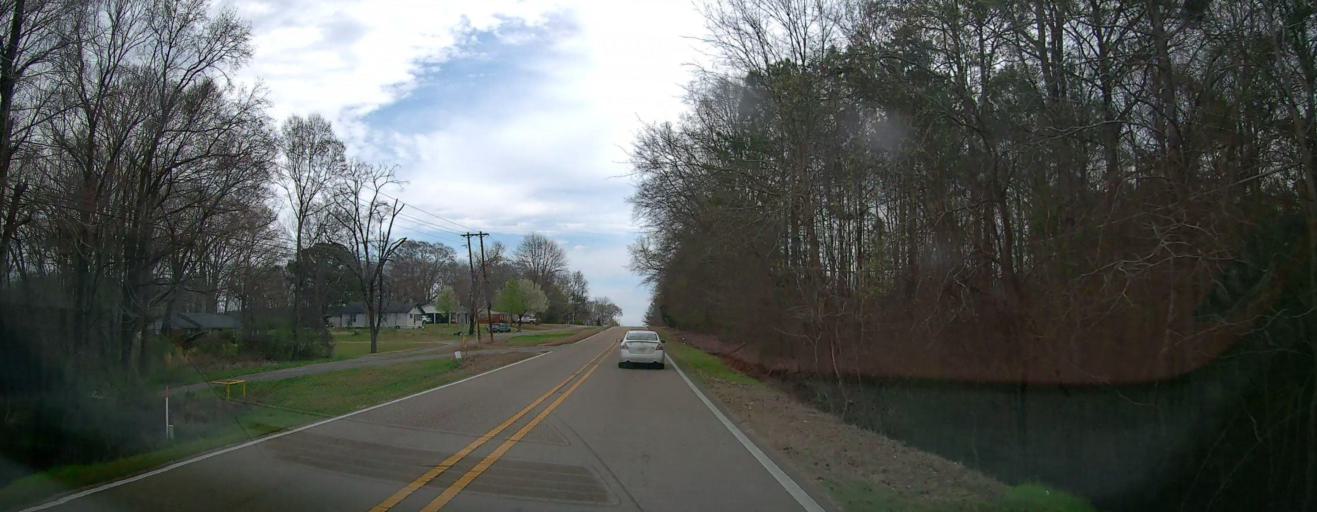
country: US
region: Mississippi
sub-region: Itawamba County
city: Fulton
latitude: 34.2715
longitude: -88.3397
